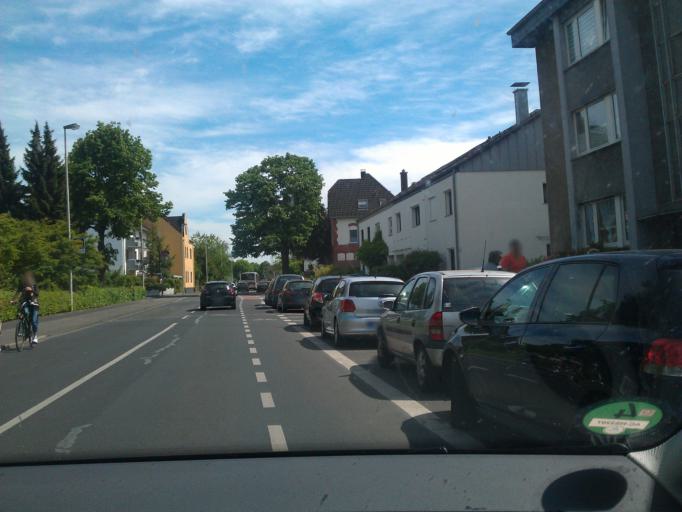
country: DE
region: North Rhine-Westphalia
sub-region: Regierungsbezirk Dusseldorf
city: Hilden
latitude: 51.1623
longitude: 6.9419
